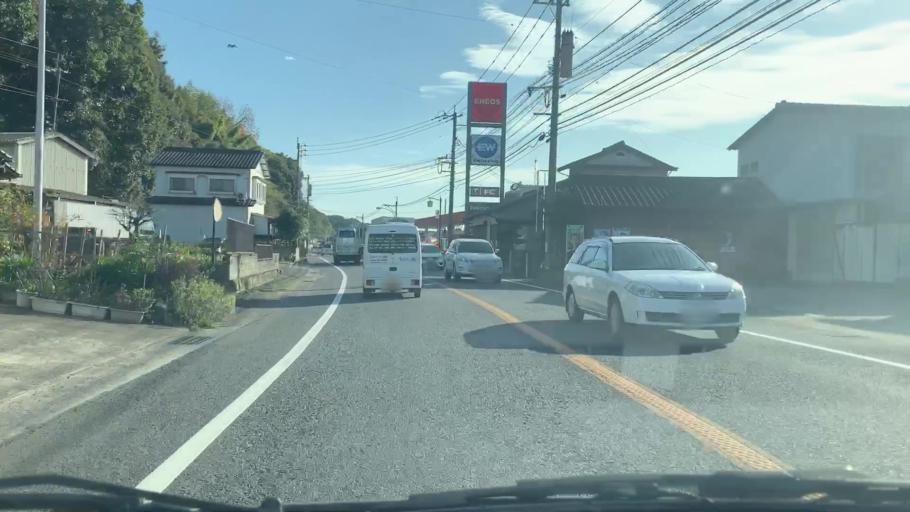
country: JP
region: Saga Prefecture
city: Takeocho-takeo
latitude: 33.2169
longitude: 130.0796
